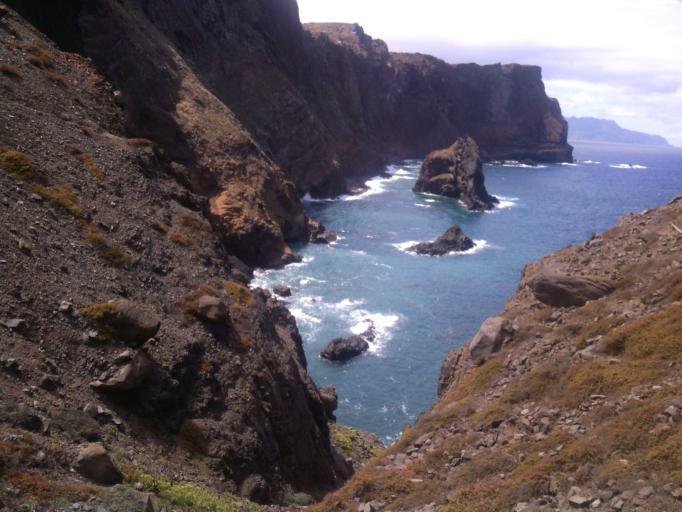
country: PT
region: Madeira
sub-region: Machico
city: Canical
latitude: 32.7488
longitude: -16.6974
